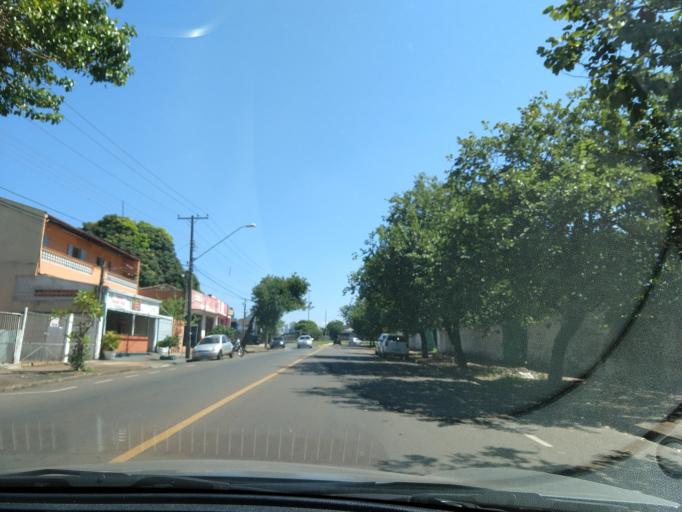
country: BR
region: Parana
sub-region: Londrina
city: Londrina
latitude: -23.3036
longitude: -51.1443
